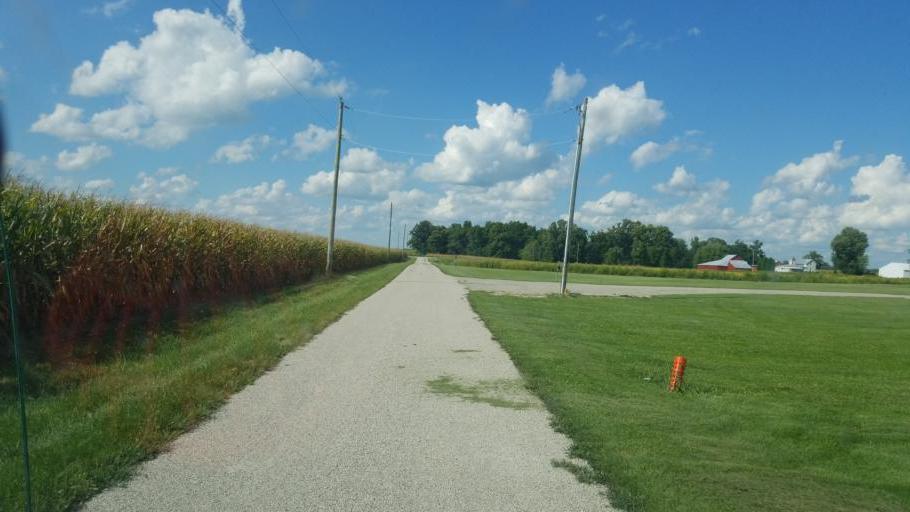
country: US
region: Ohio
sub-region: Union County
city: Richwood
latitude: 40.5109
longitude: -83.3706
